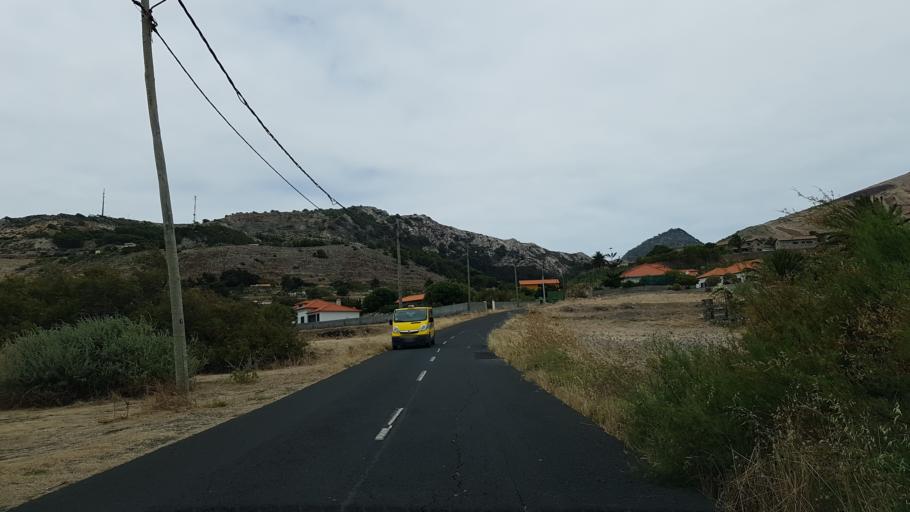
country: PT
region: Madeira
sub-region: Porto Santo
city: Vila de Porto Santo
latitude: 33.0736
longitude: -16.3106
